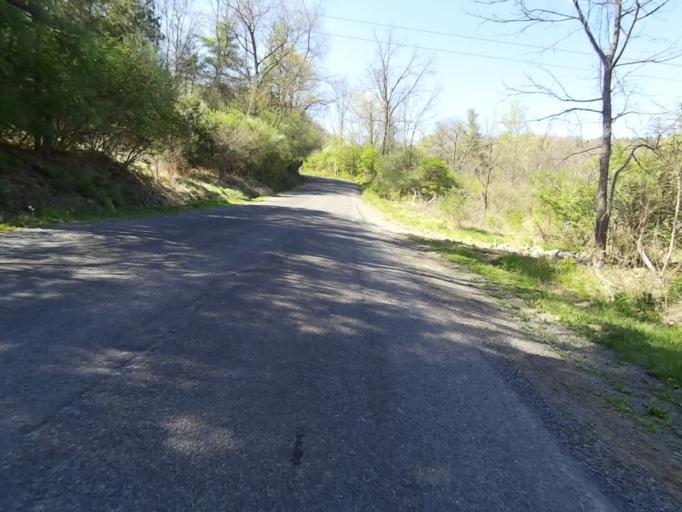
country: US
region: Pennsylvania
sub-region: Centre County
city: Houserville
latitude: 40.8905
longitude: -77.8490
